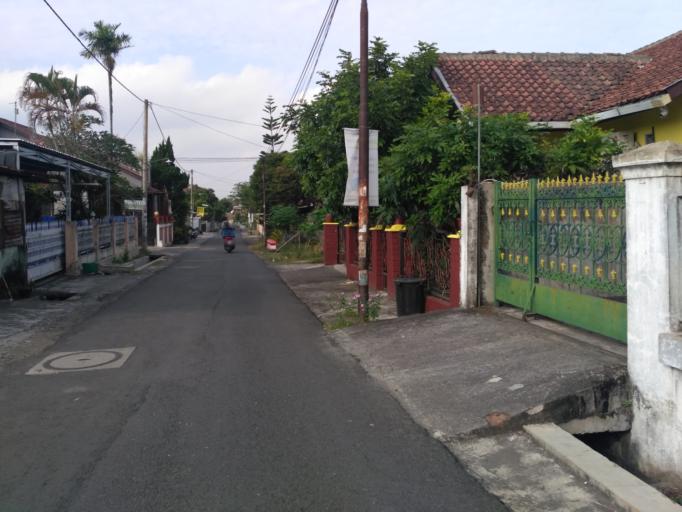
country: ID
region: Daerah Istimewa Yogyakarta
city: Melati
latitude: -7.7358
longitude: 110.3899
